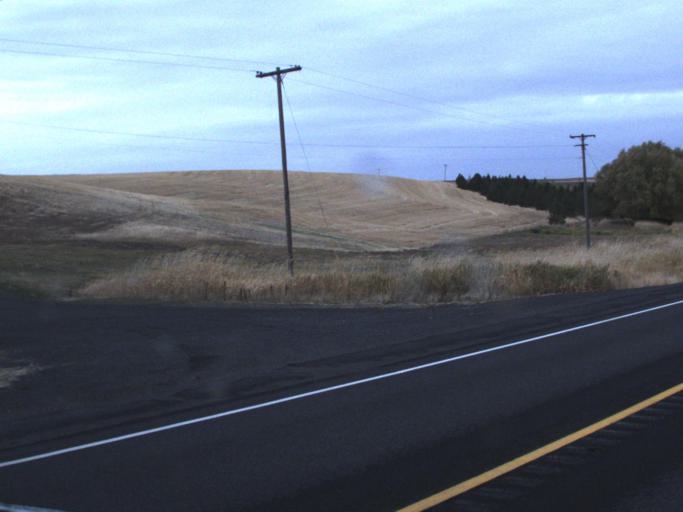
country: US
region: Washington
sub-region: Whitman County
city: Pullman
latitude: 46.7463
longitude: -117.2343
